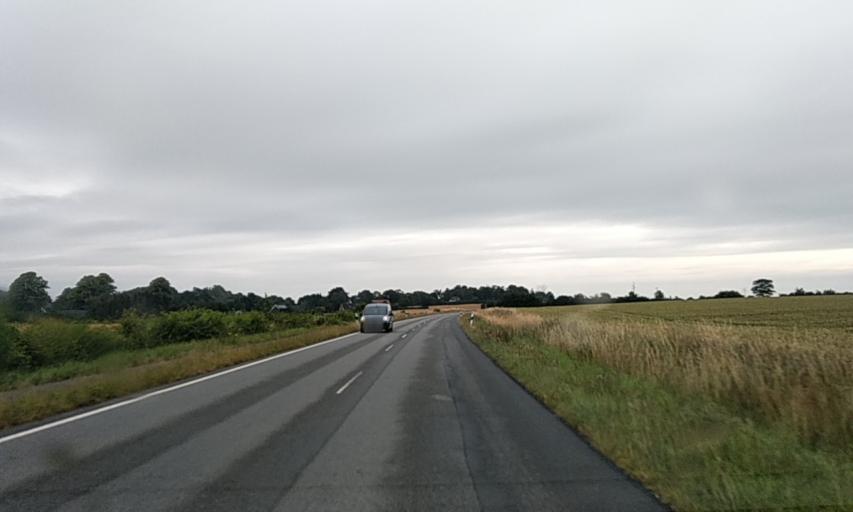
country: DE
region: Schleswig-Holstein
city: Struxdorf
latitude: 54.6258
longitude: 9.6313
